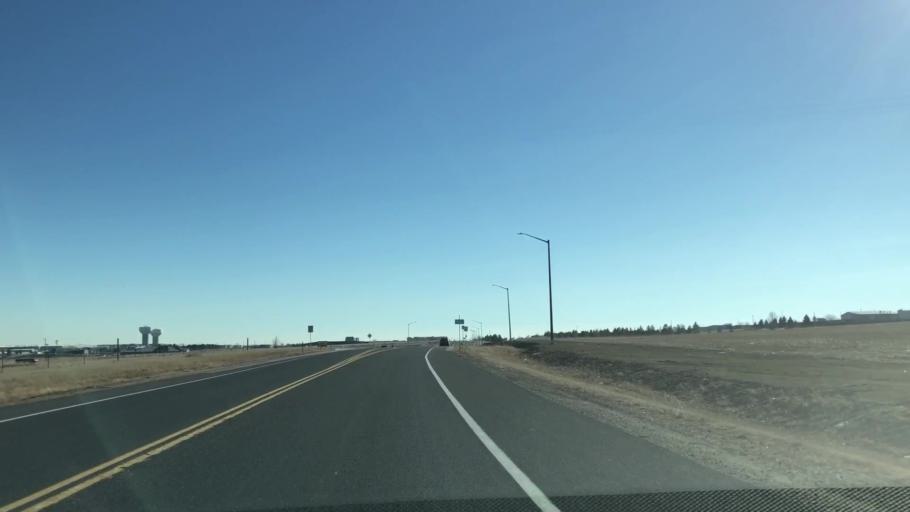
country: US
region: Colorado
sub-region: Weld County
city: Windsor
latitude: 40.4529
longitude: -104.9824
